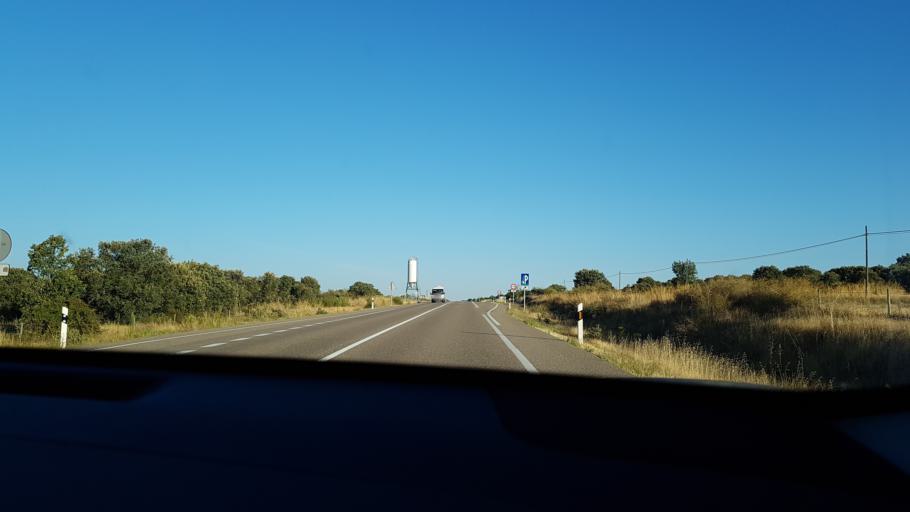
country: ES
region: Castille and Leon
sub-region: Provincia de Zamora
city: Fonfria
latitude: 41.6452
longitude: -6.1594
